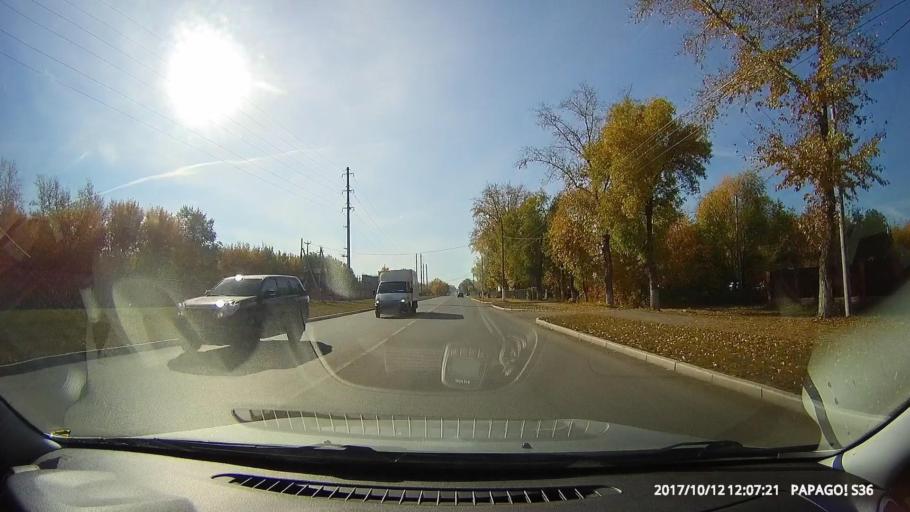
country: RU
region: Samara
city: Chapayevsk
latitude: 52.9676
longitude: 49.7018
